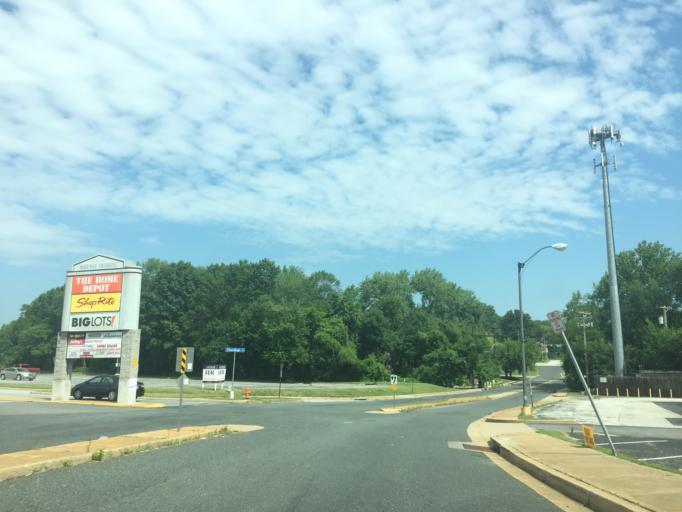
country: US
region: Maryland
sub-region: Baltimore County
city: Parkville
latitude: 39.3724
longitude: -76.5596
